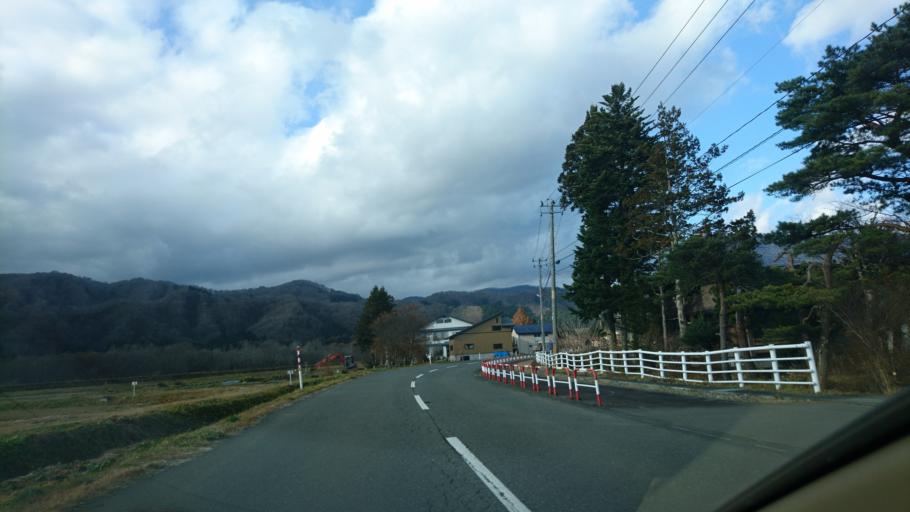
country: JP
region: Akita
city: Yokotemachi
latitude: 39.4360
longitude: 140.7588
